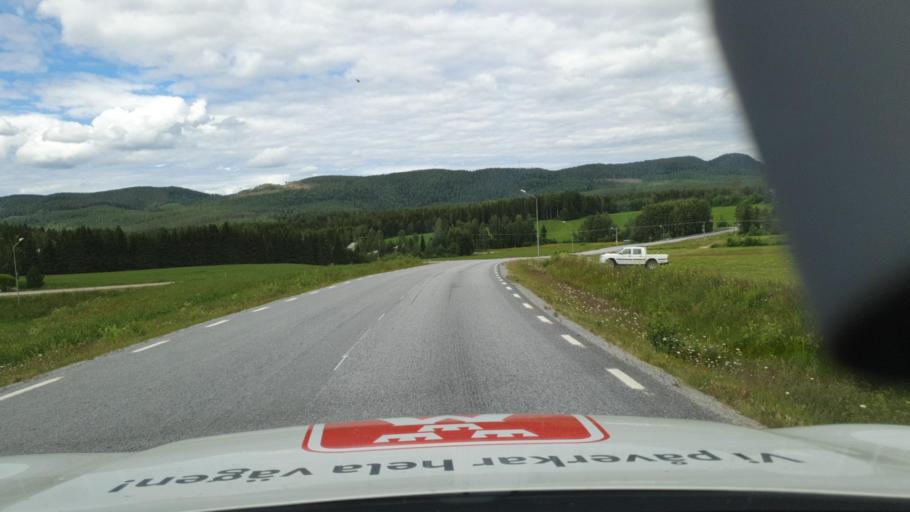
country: SE
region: Vaesterbotten
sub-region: Bjurholms Kommun
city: Bjurholm
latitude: 63.9107
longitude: 19.0864
